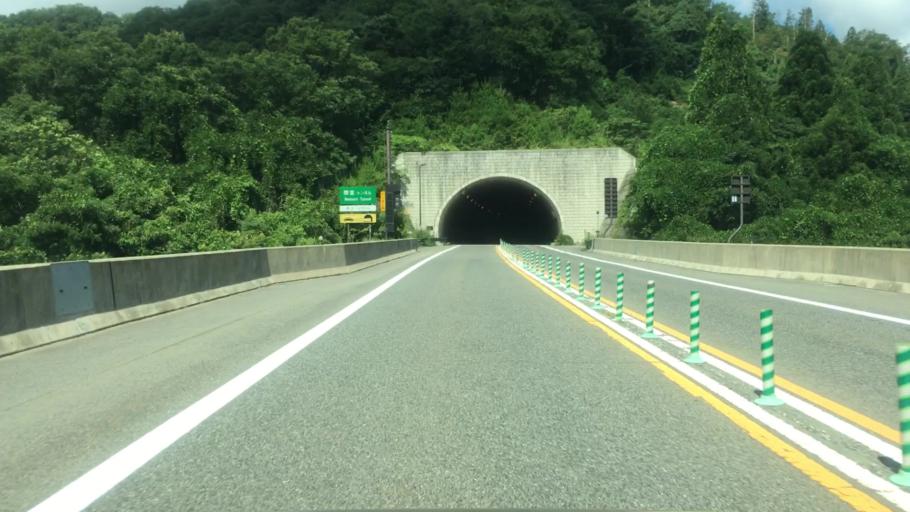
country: JP
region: Hyogo
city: Toyooka
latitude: 35.6283
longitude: 134.6071
